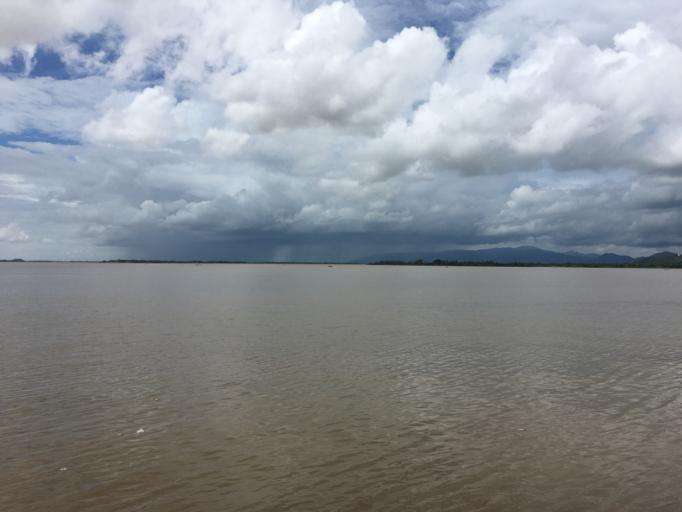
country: MM
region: Mon
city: Mawlamyine
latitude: 16.4988
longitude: 97.6186
